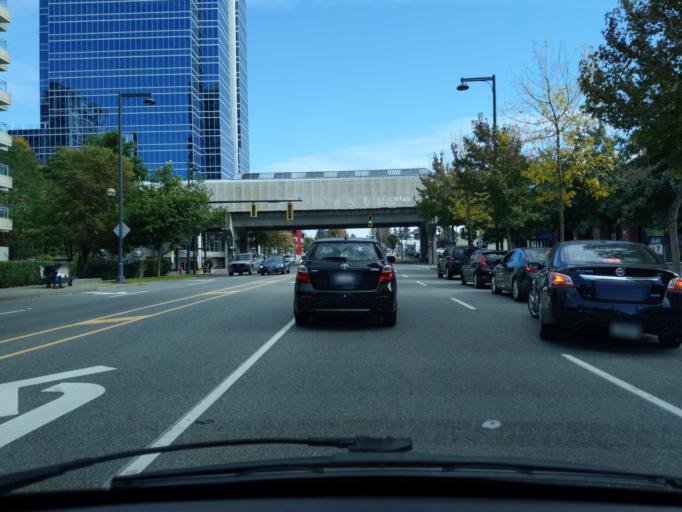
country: CA
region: British Columbia
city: New Westminster
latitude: 49.1989
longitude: -122.8520
